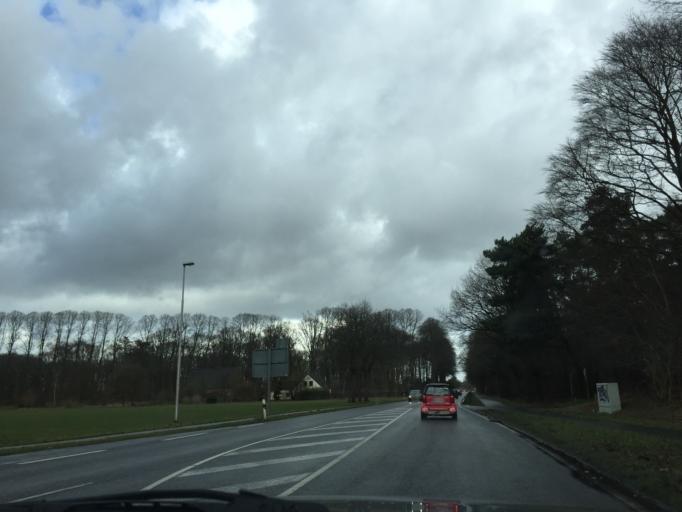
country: DE
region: North Rhine-Westphalia
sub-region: Regierungsbezirk Dusseldorf
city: Emmerich
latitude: 51.8515
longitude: 6.2415
